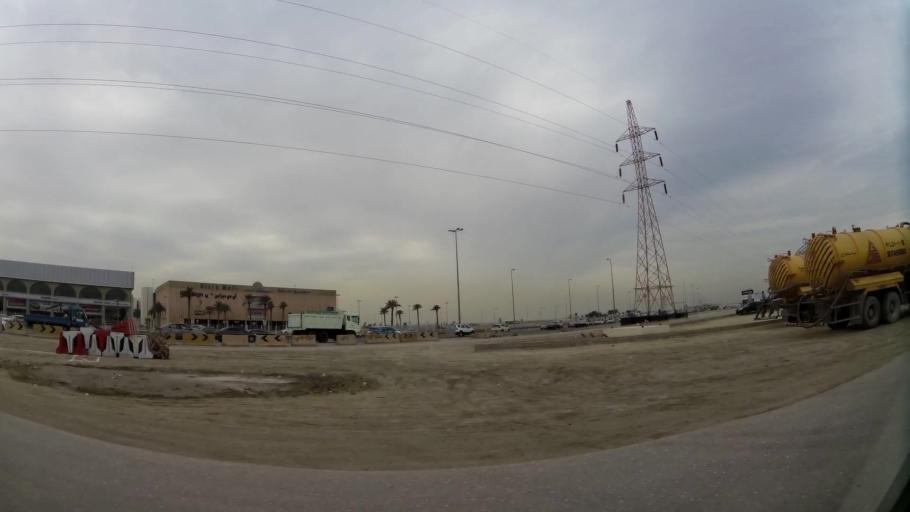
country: BH
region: Northern
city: Sitrah
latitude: 26.1706
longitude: 50.6035
